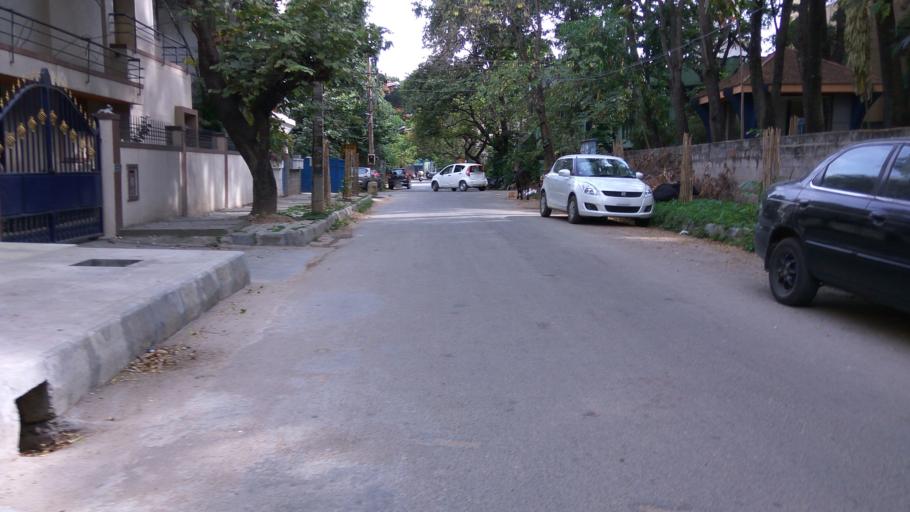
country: IN
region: Karnataka
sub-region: Bangalore Urban
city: Bangalore
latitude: 12.9720
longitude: 77.6449
